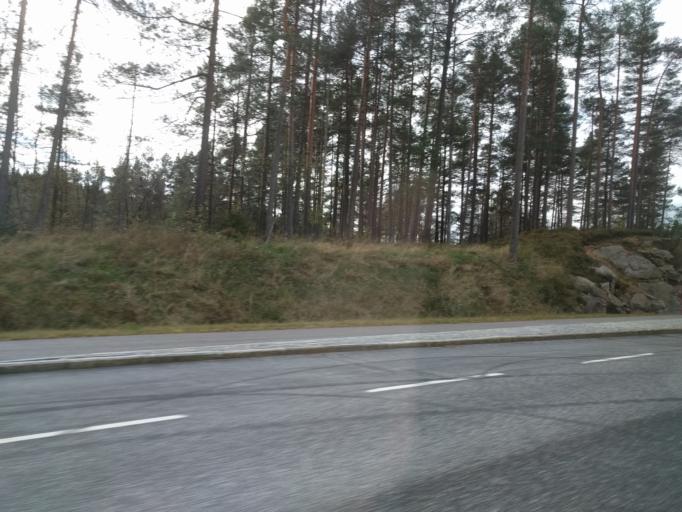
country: NO
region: Vest-Agder
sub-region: Songdalen
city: Nodeland
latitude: 58.2833
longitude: 7.8378
